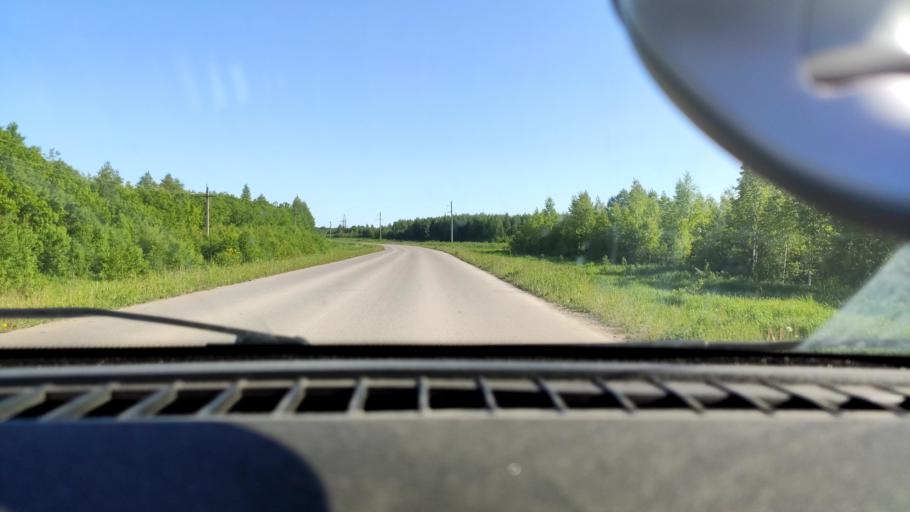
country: RU
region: Perm
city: Polazna
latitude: 58.2028
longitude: 56.5317
